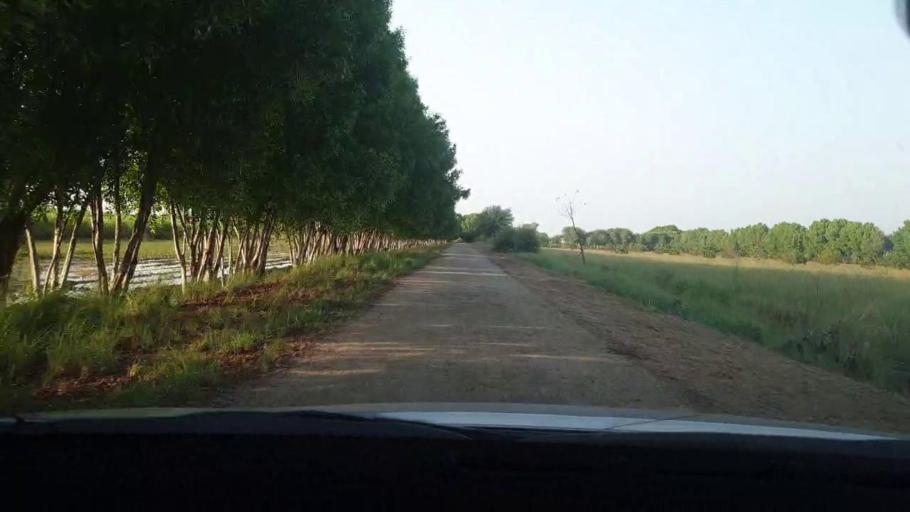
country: PK
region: Sindh
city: Pithoro
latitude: 25.6139
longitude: 69.4423
